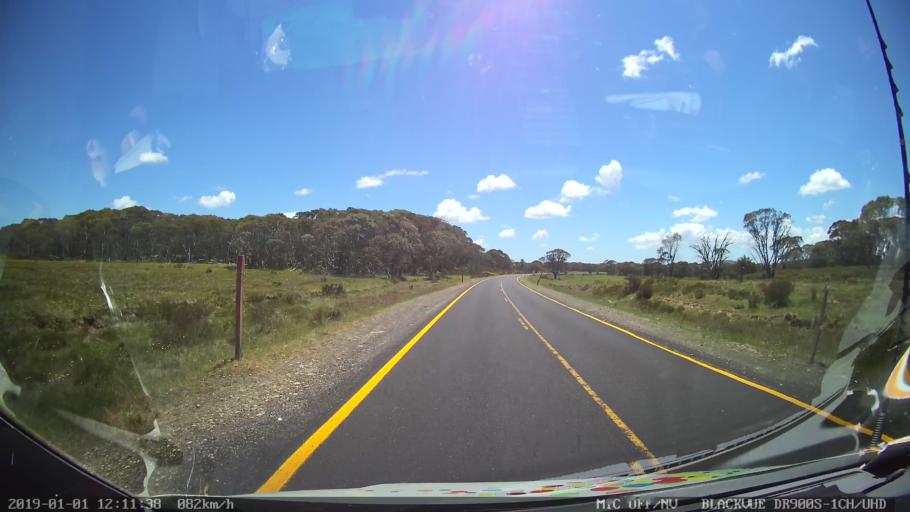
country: AU
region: New South Wales
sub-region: Tumut Shire
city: Tumut
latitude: -35.7819
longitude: 148.5084
